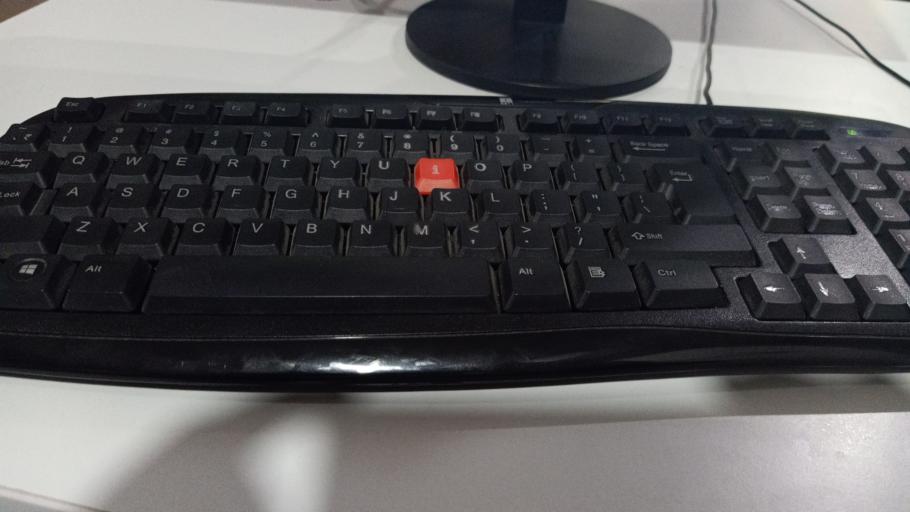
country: IN
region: Telangana
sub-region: Rangareddi
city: Kukatpalli
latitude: 17.4997
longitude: 78.4013
